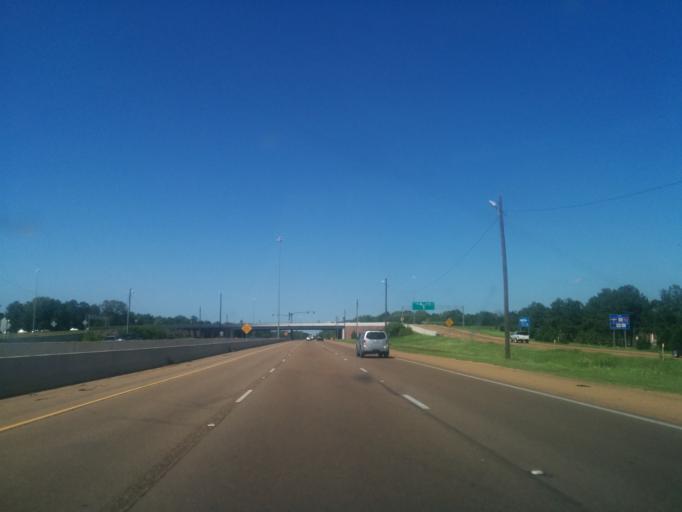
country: US
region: Mississippi
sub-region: Madison County
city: Madison
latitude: 32.4674
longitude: -90.1364
